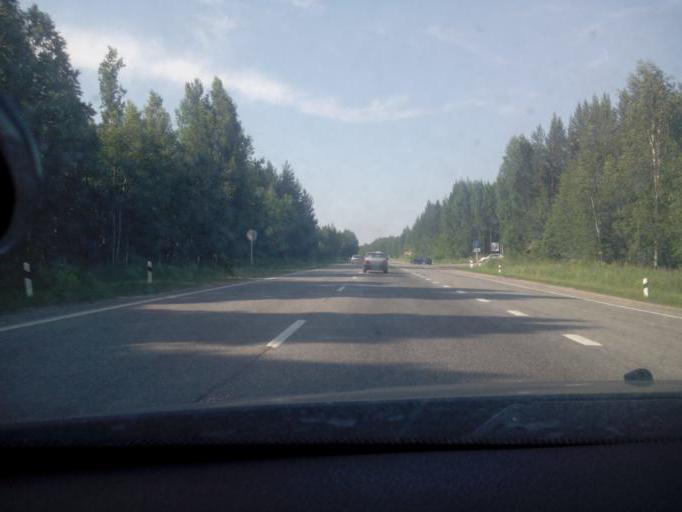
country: RU
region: Sverdlovsk
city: Verkh-Neyvinskiy
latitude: 57.2749
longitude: 60.2958
